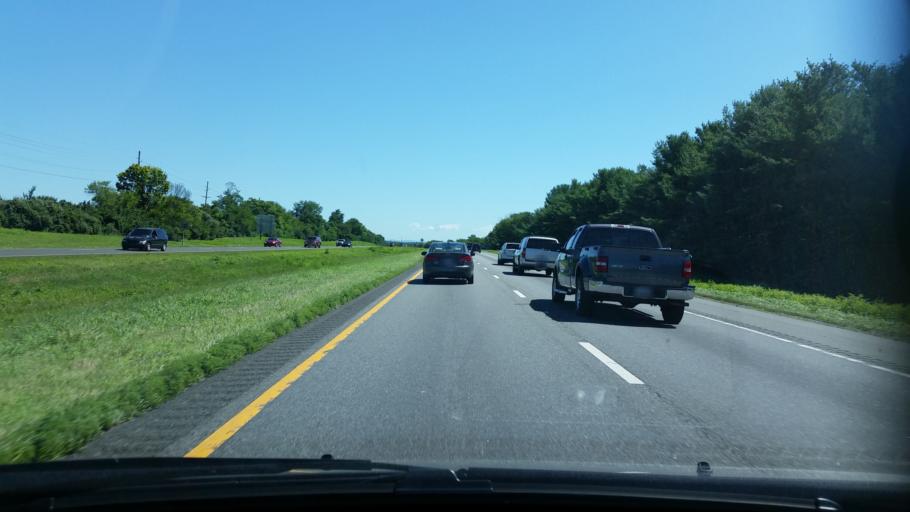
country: US
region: Virginia
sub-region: City of Winchester
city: Winchester
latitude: 39.2354
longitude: -78.1275
